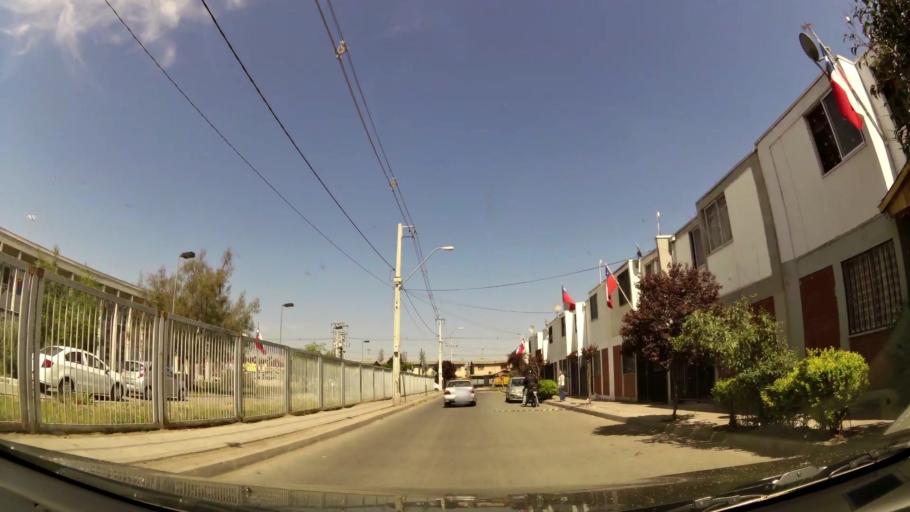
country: CL
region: Santiago Metropolitan
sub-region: Provincia de Santiago
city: Lo Prado
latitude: -33.3974
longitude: -70.7501
